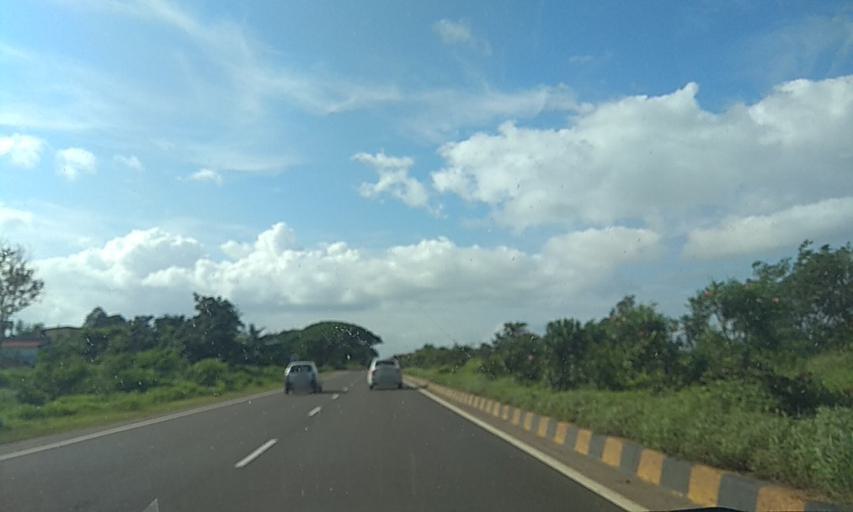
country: IN
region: Maharashtra
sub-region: Kolhapur
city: Kodoli
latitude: 17.0164
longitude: 74.2548
